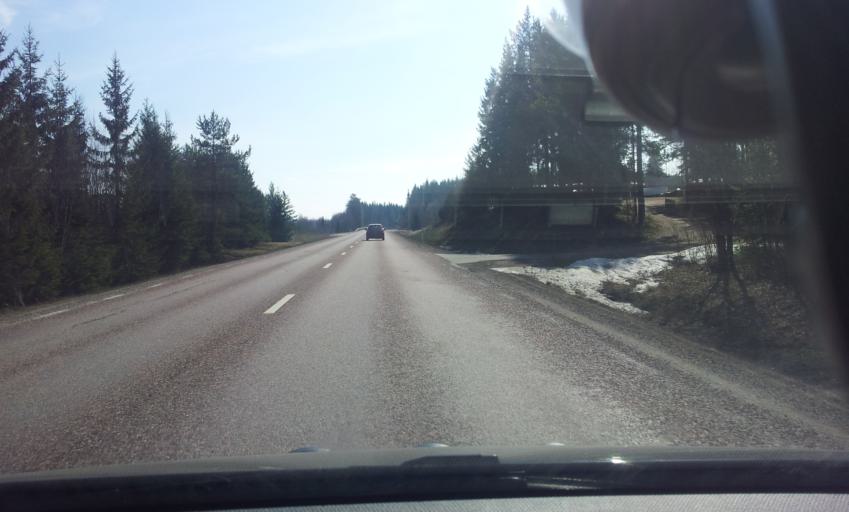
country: SE
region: Gaevleborg
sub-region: Ljusdals Kommun
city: Jaervsoe
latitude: 61.7763
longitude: 16.1478
